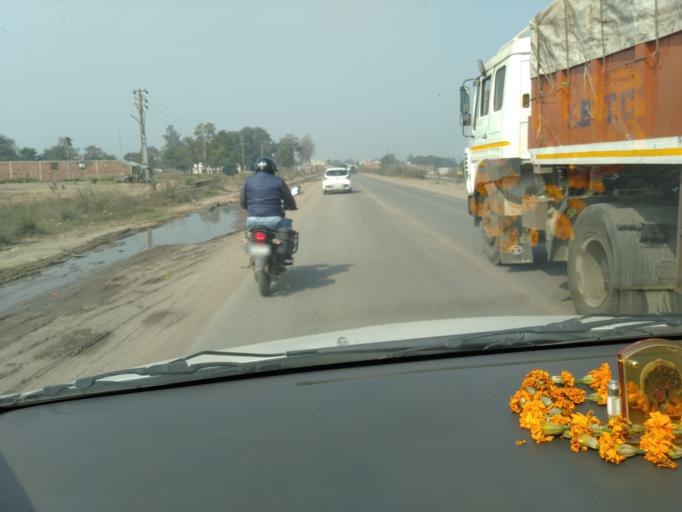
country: IN
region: Bihar
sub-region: Rohtas
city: Dehri
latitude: 24.9185
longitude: 84.1507
